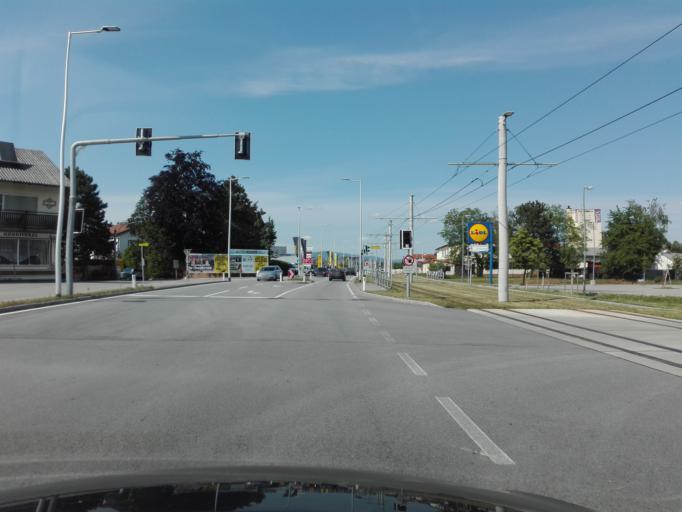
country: AT
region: Upper Austria
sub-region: Politischer Bezirk Linz-Land
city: Traun
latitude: 48.2295
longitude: 14.2337
